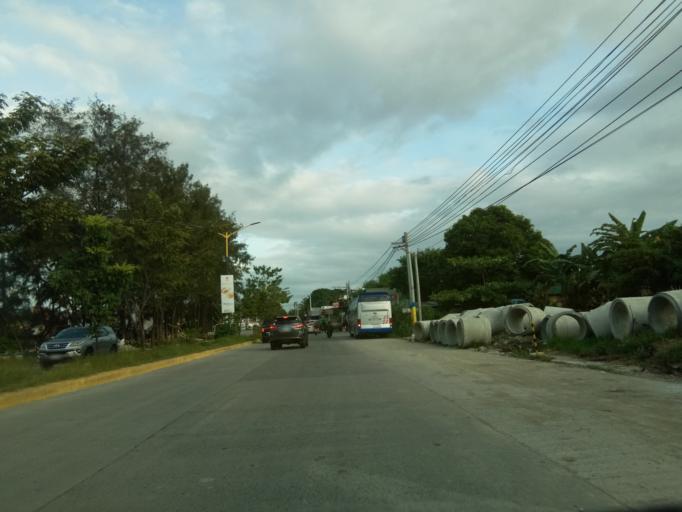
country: PH
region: Calabarzon
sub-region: Province of Cavite
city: Imus
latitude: 14.3871
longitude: 120.9733
